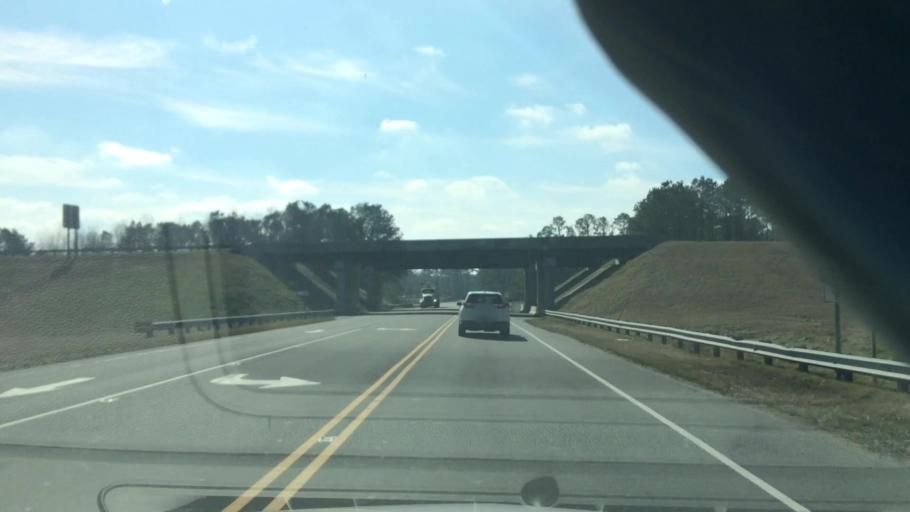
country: US
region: North Carolina
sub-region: Duplin County
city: Wallace
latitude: 34.7558
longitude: -77.9501
